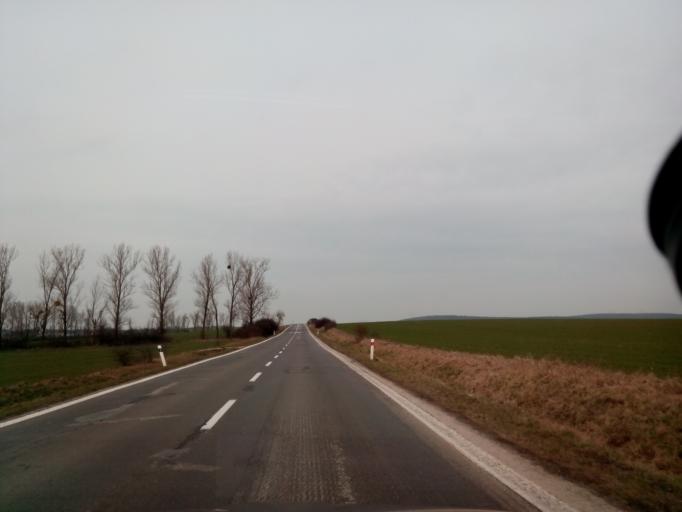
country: HU
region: Borsod-Abauj-Zemplen
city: Satoraljaujhely
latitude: 48.4738
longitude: 21.6412
